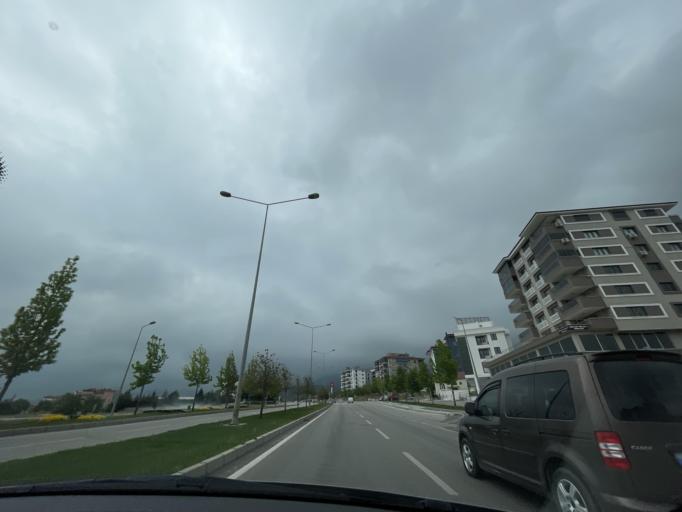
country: TR
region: Denizli
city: Denizli
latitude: 37.7316
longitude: 29.1470
